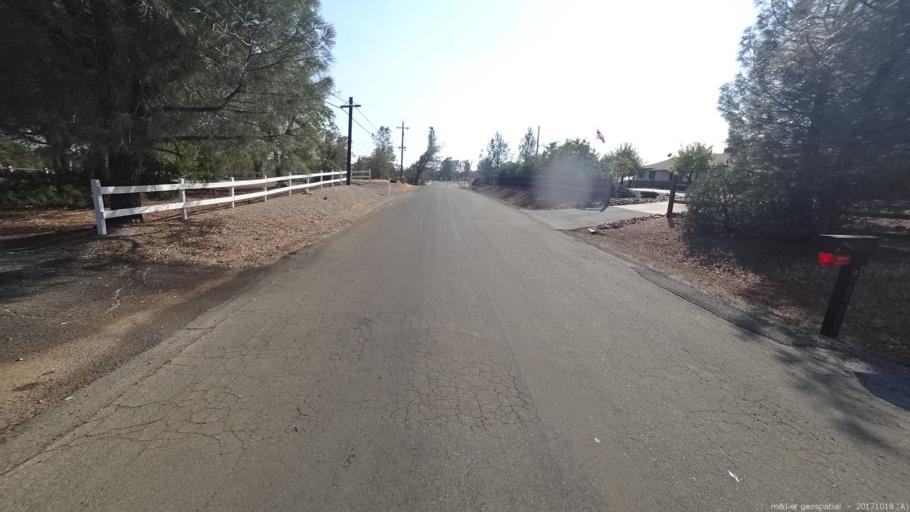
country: US
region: California
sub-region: Shasta County
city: Palo Cedro
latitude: 40.5549
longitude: -122.2767
